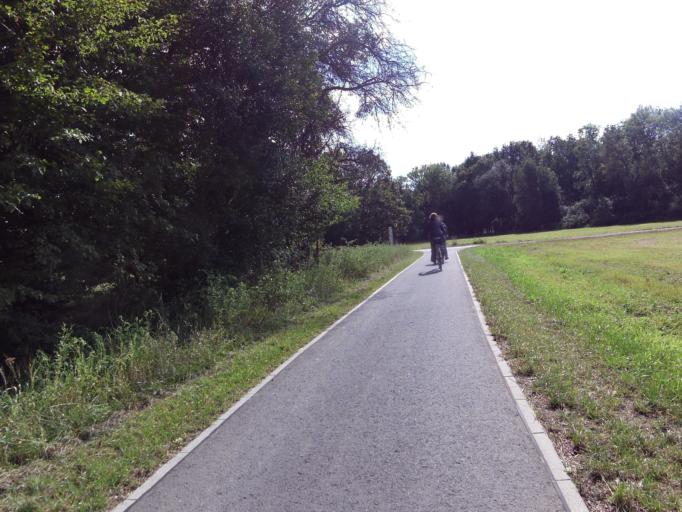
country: DE
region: Saxony-Anhalt
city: Vockerode
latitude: 51.8580
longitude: 12.3302
